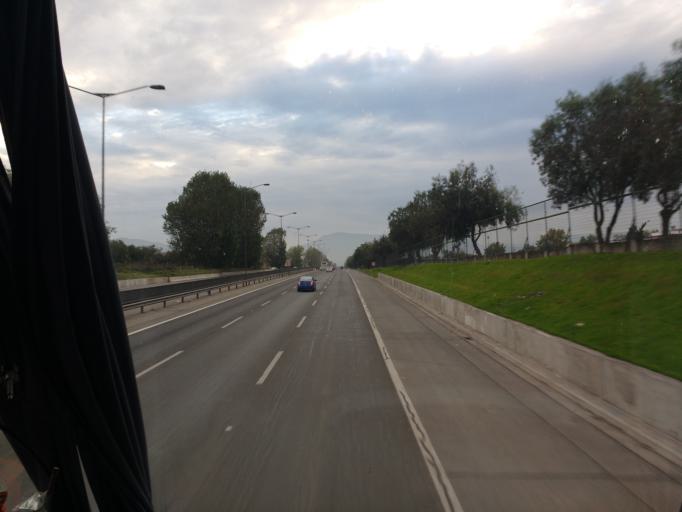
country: CL
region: Santiago Metropolitan
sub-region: Provincia de Santiago
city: Lo Prado
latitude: -33.4530
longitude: -70.7409
